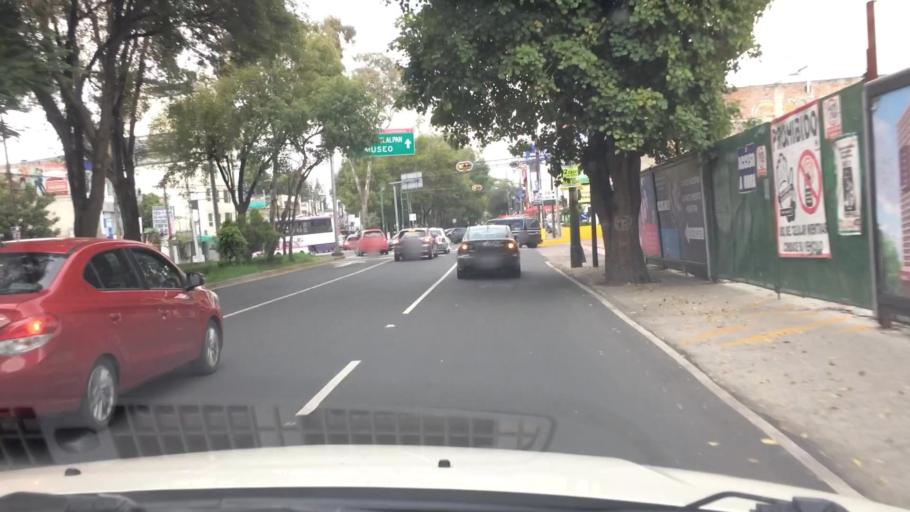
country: MX
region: Mexico City
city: Coyoacan
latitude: 19.3375
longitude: -99.1474
